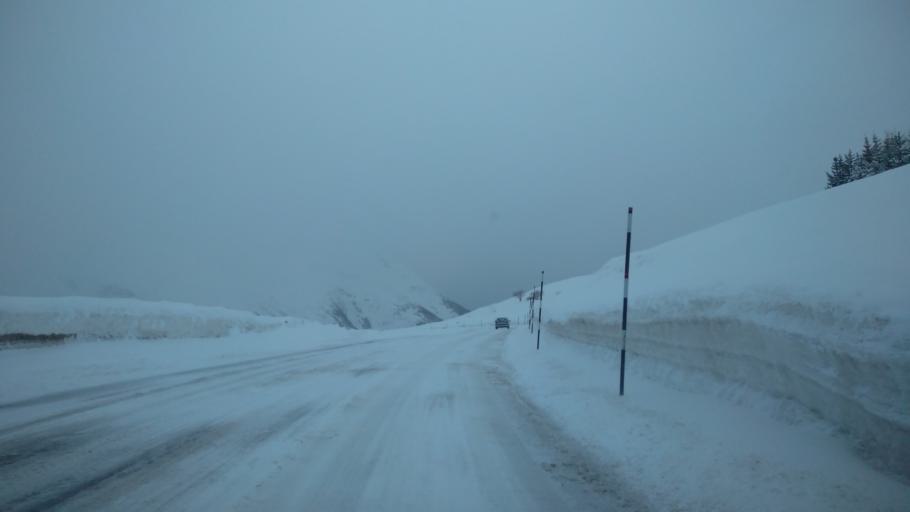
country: FR
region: Provence-Alpes-Cote d'Azur
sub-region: Departement des Hautes-Alpes
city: Le Monetier-les-Bains
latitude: 45.0329
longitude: 6.3951
